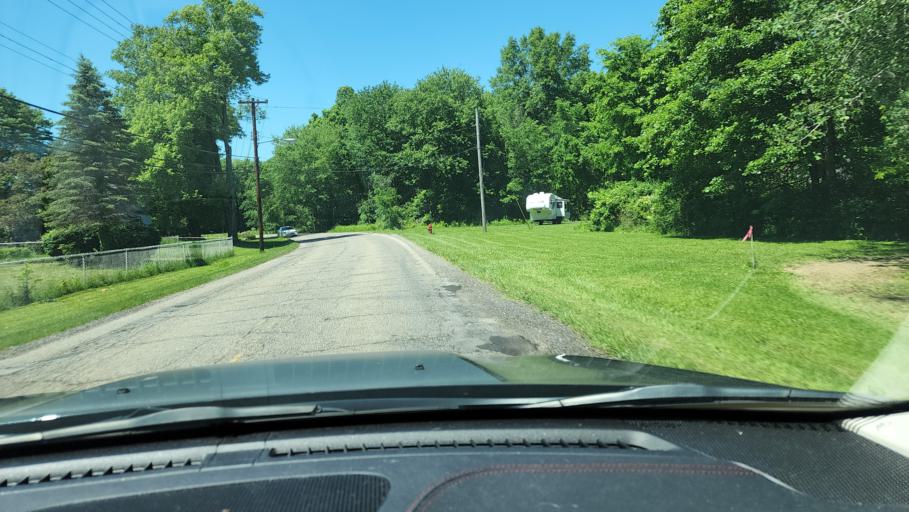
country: US
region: Ohio
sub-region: Trumbull County
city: Niles
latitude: 41.1664
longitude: -80.7798
